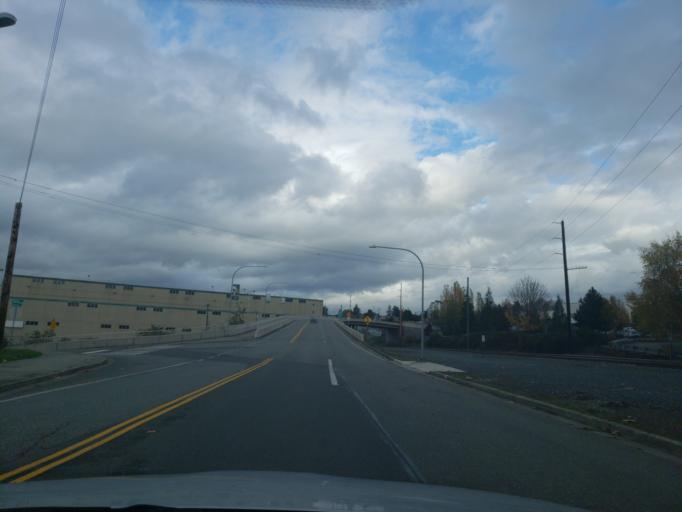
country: US
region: Washington
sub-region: Snohomish County
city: Everett
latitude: 47.9804
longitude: -122.2170
